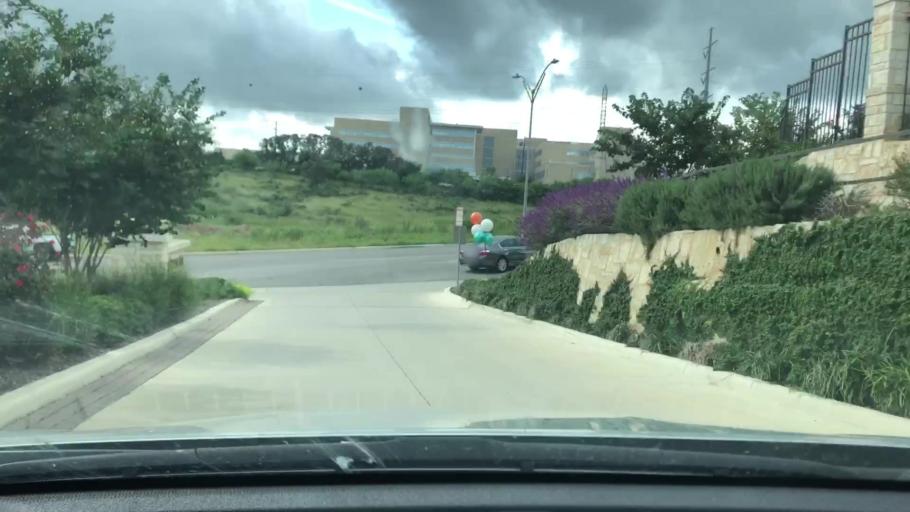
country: US
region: Texas
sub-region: Bexar County
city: Hollywood Park
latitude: 29.6191
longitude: -98.4745
